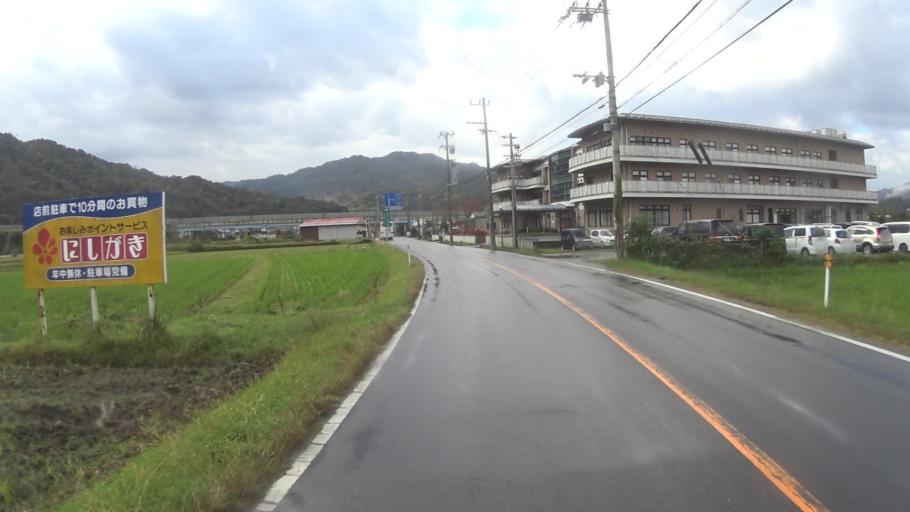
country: JP
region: Kyoto
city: Miyazu
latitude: 35.5537
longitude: 135.1603
